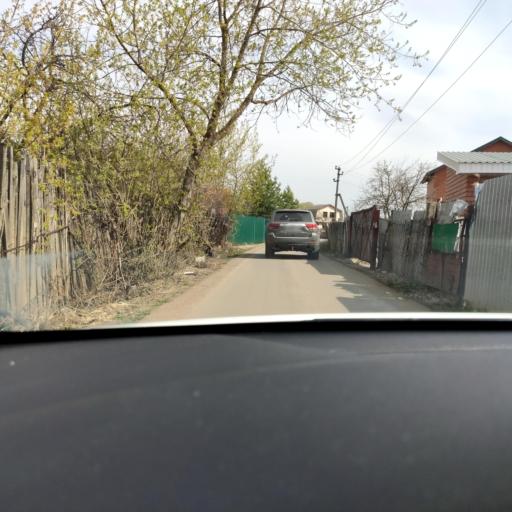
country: RU
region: Tatarstan
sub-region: Gorod Kazan'
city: Kazan
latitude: 55.8512
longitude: 49.1661
